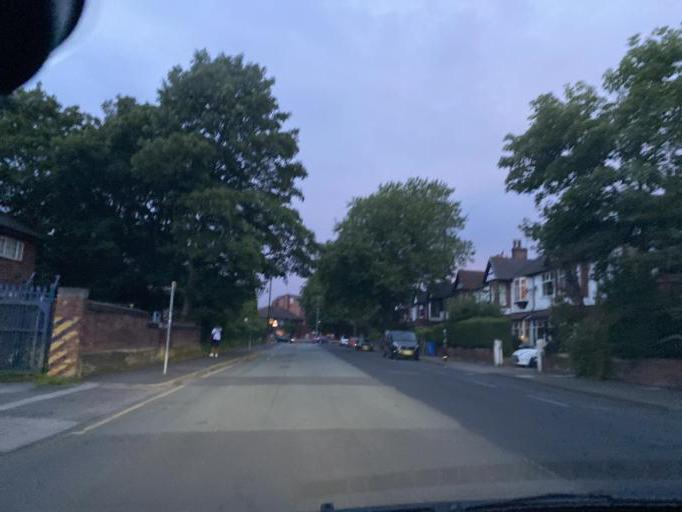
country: GB
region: England
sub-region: Manchester
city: Chorlton cum Hardy
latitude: 53.4514
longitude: -2.2704
